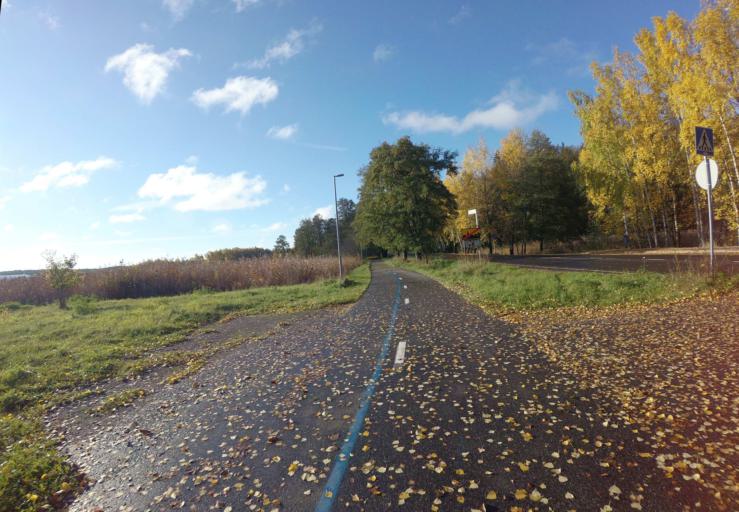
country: FI
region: Varsinais-Suomi
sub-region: Turku
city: Raisio
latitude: 60.4408
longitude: 22.2050
